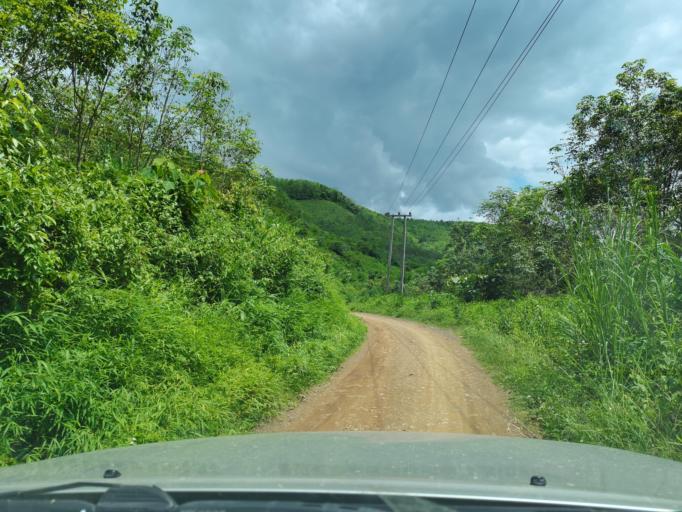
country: LA
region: Loungnamtha
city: Muang Long
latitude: 20.7173
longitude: 101.0145
